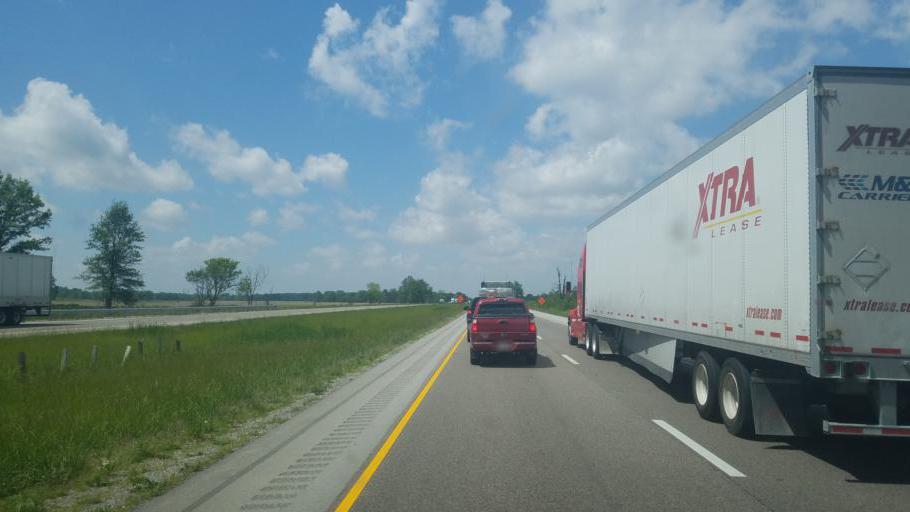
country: US
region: Illinois
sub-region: Cumberland County
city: Toledo
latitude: 39.2287
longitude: -88.2205
